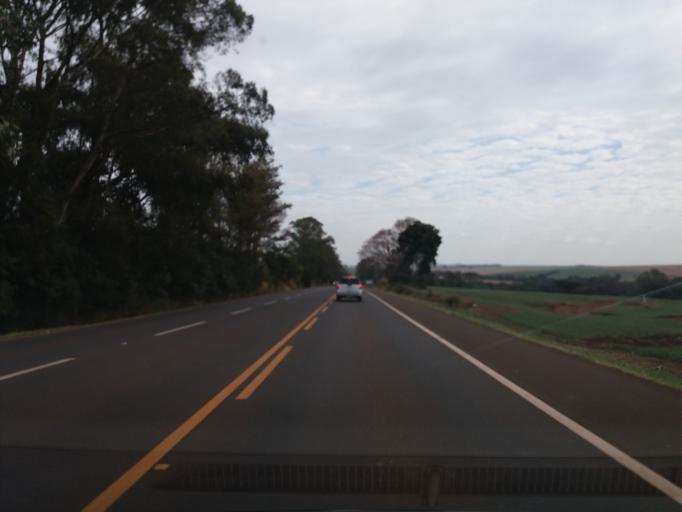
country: BR
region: Parana
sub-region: Campo Mourao
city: Campo Mourao
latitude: -24.3154
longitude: -52.6202
